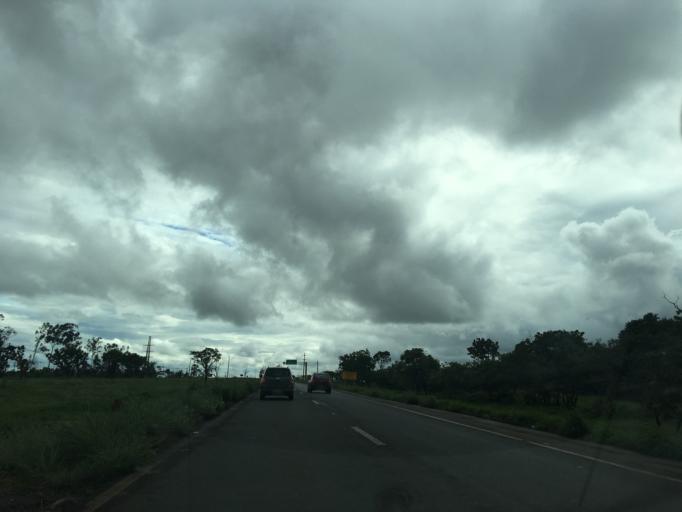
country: BR
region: Federal District
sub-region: Brasilia
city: Brasilia
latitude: -15.9246
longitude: -47.8304
